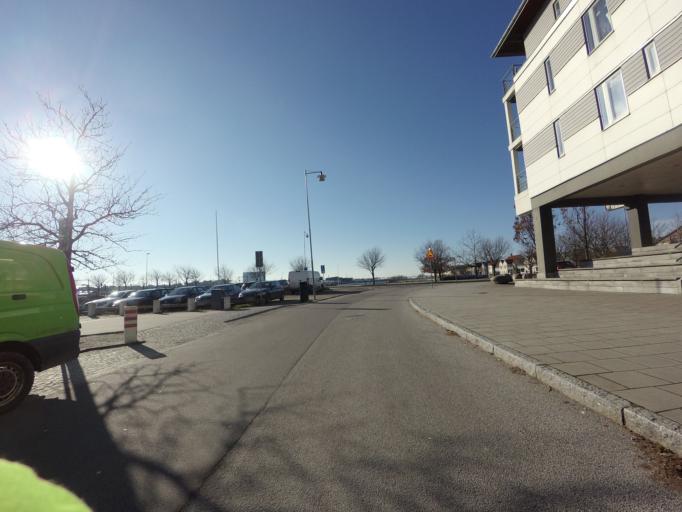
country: SE
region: Skane
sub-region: Malmo
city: Bunkeflostrand
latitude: 55.5894
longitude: 12.9230
